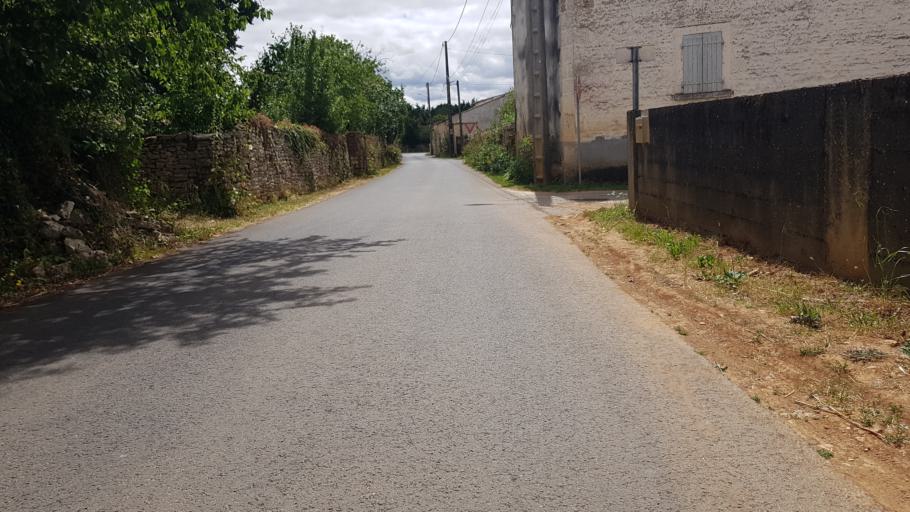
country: FR
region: Poitou-Charentes
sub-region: Departement des Deux-Sevres
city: Vouille
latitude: 46.3053
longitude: -0.3345
